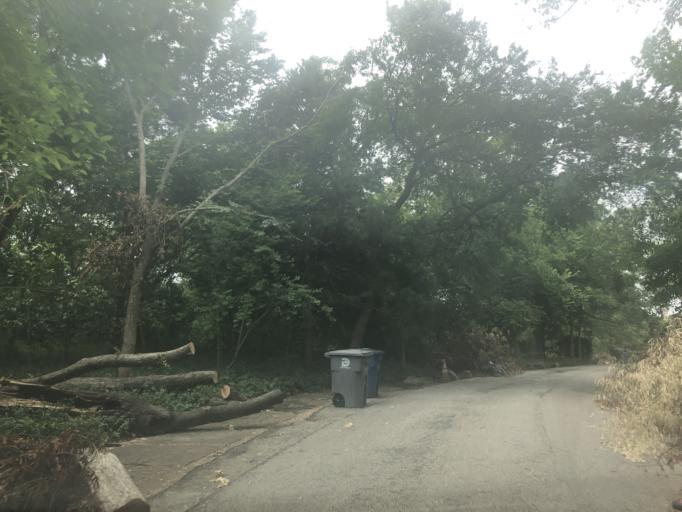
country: US
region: Texas
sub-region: Dallas County
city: University Park
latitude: 32.8587
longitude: -96.8355
